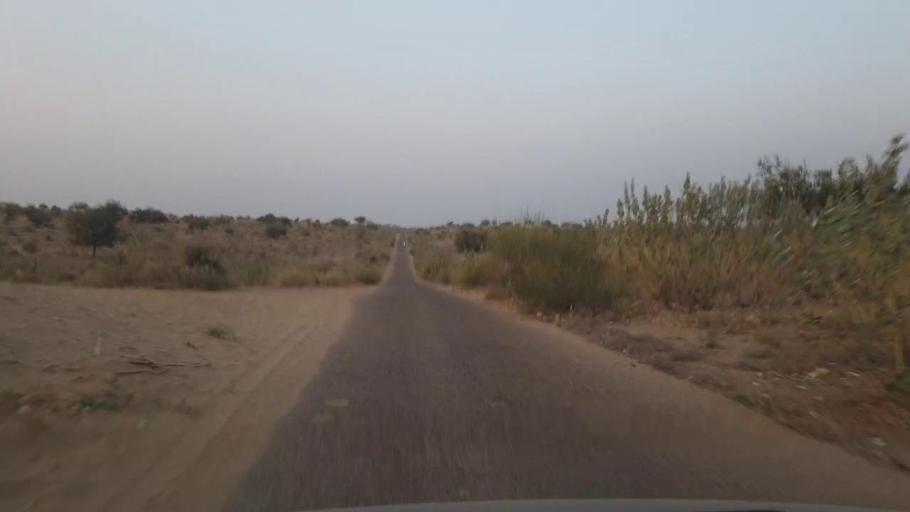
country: PK
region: Sindh
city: Umarkot
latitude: 25.3275
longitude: 70.0576
